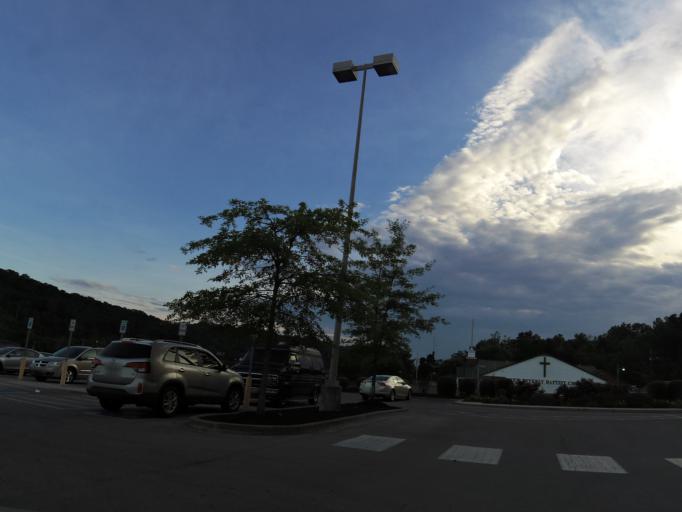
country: US
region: Tennessee
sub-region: Knox County
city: Knoxville
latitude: 36.0361
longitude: -83.8900
